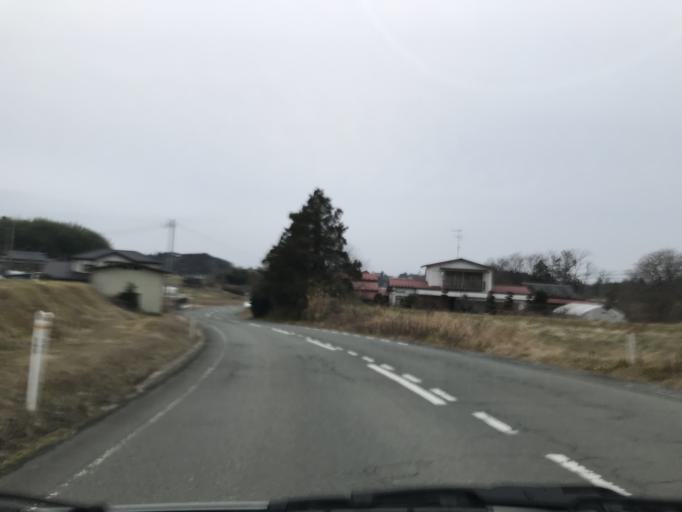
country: JP
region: Miyagi
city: Kogota
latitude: 38.6822
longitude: 141.0966
